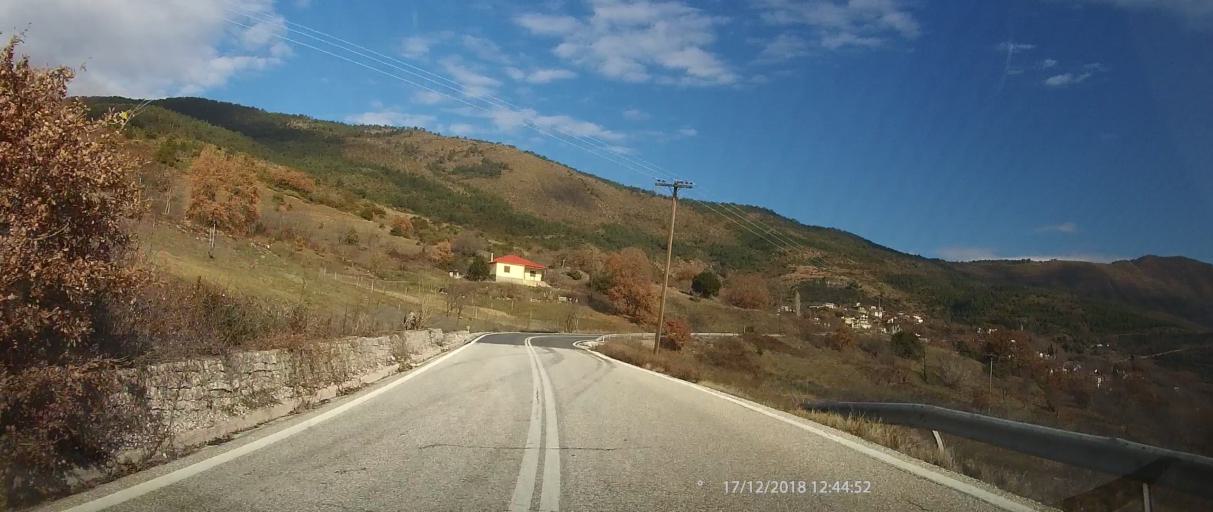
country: GR
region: Epirus
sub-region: Nomos Ioanninon
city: Metsovo
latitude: 39.7846
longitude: 21.4050
